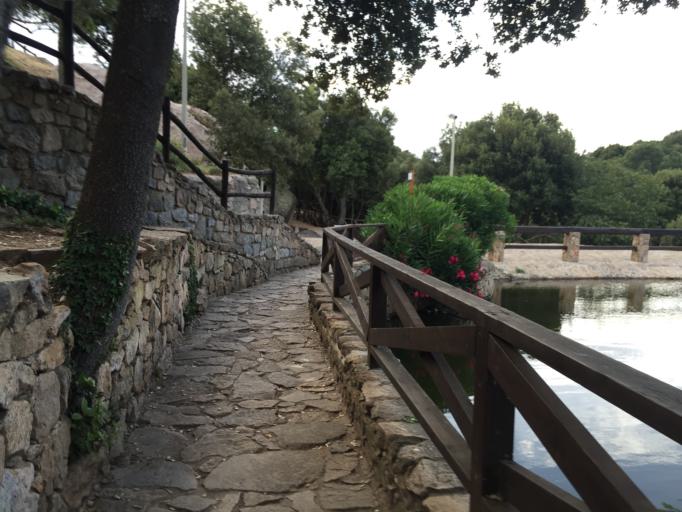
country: IT
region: Sardinia
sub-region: Provincia di Olbia-Tempio
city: Aggius
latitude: 40.9281
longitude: 9.0587
